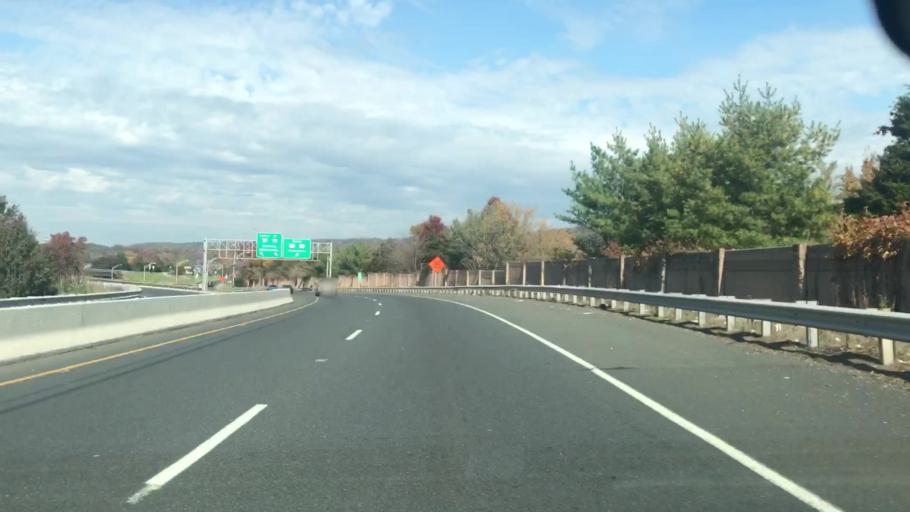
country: US
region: New Jersey
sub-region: Somerset County
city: Green Knoll
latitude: 40.5954
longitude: -74.6228
